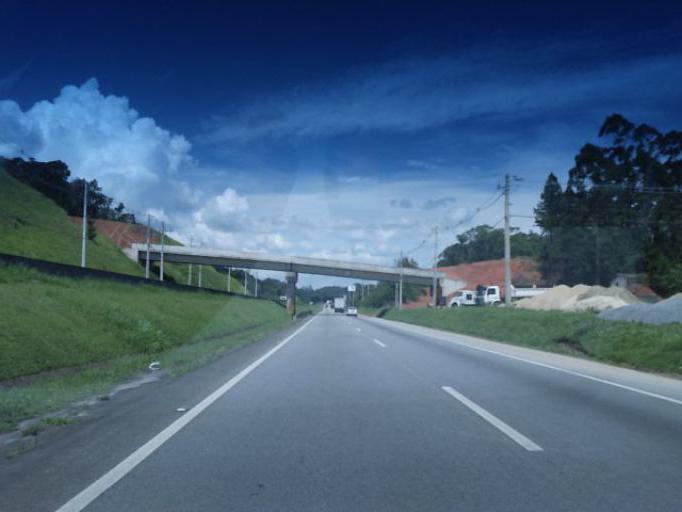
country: BR
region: Sao Paulo
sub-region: Juquitiba
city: Juquitiba
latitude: -23.9349
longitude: -47.0240
